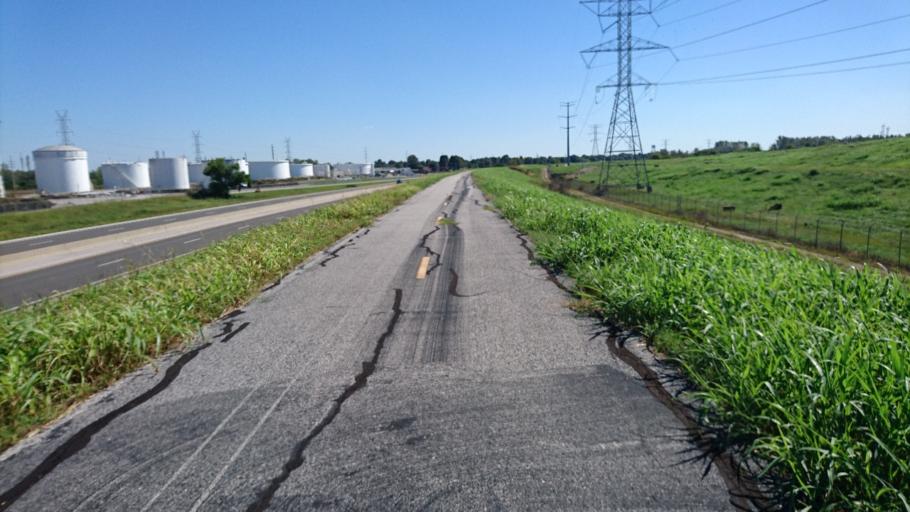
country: US
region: Illinois
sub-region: Madison County
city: Hartford
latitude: 38.8469
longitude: -90.0995
